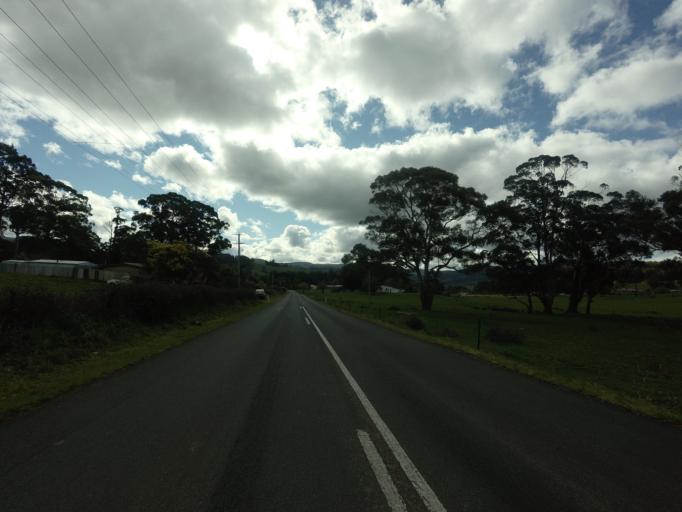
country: AU
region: Tasmania
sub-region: Huon Valley
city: Geeveston
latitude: -43.1810
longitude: 146.9275
